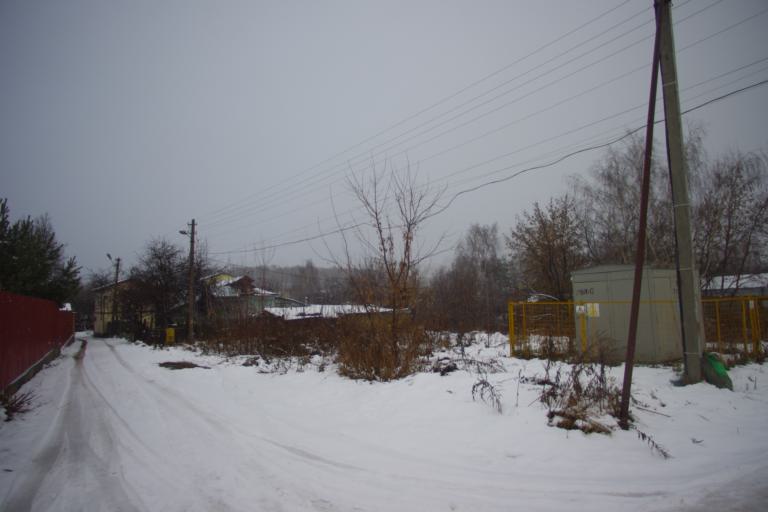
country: RU
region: Moskovskaya
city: Arkhangel'skoye
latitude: 55.8013
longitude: 37.3133
